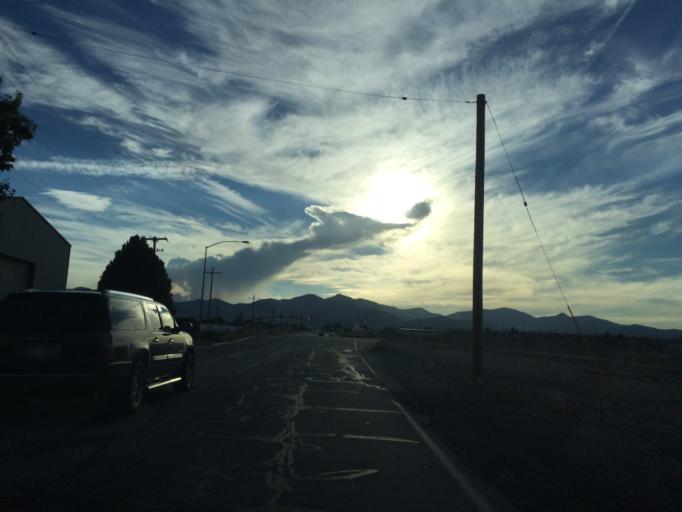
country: US
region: Utah
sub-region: Salt Lake County
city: Oquirrh
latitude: 40.6095
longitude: -111.9947
